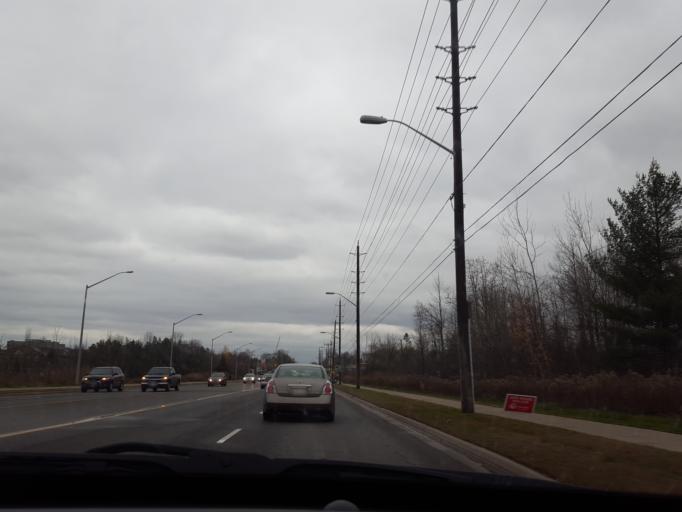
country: CA
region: Ontario
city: Ajax
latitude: 43.8478
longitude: -79.0015
